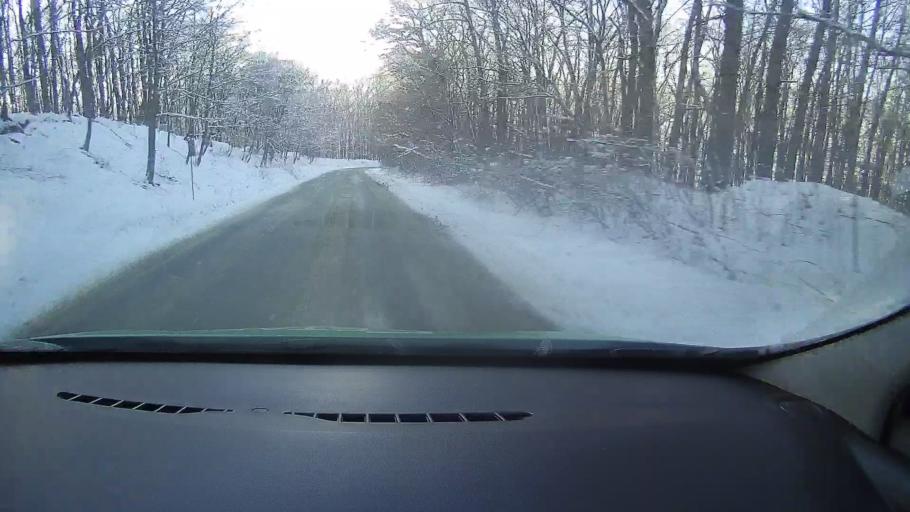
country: RO
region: Sibiu
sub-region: Oras Agnita
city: Ruja
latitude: 45.9875
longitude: 24.6729
